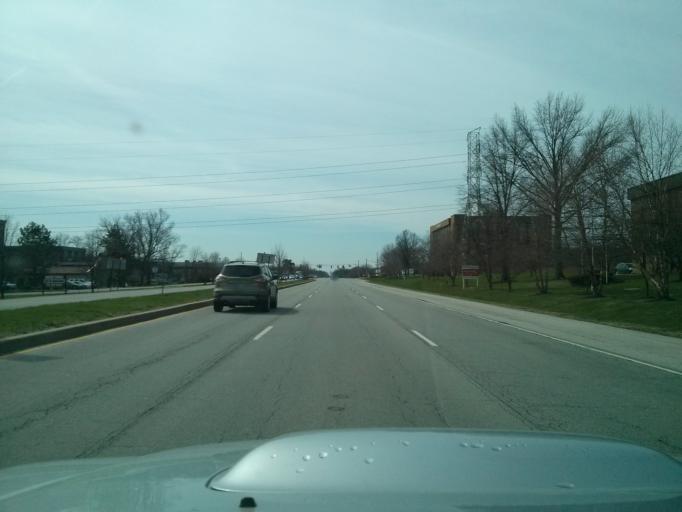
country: US
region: Indiana
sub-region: Marion County
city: Meridian Hills
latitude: 39.9223
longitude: -86.1580
